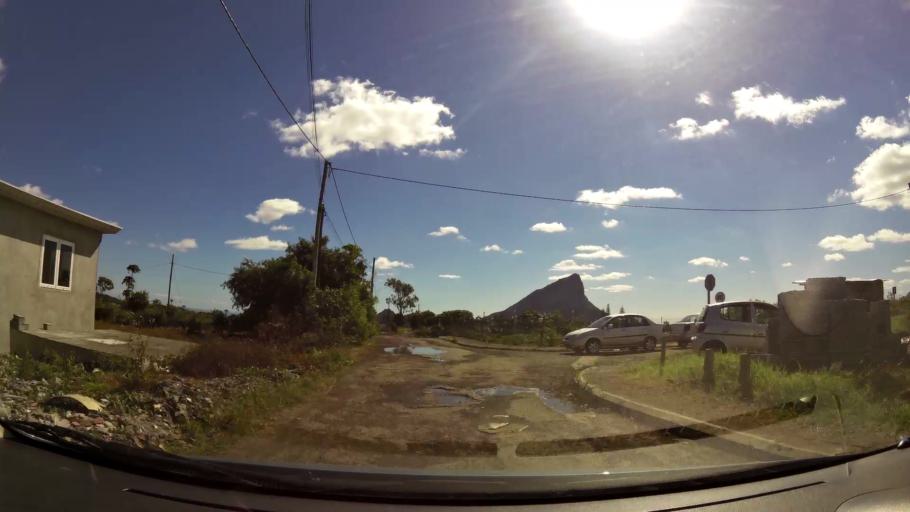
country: MU
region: Plaines Wilhems
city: Vacoas
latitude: -20.2903
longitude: 57.4731
